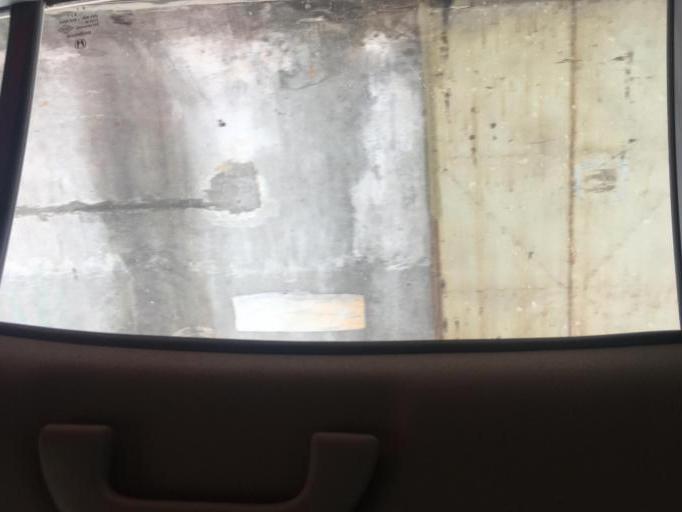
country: PK
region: Punjab
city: Lahore
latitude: 31.6149
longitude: 74.3674
